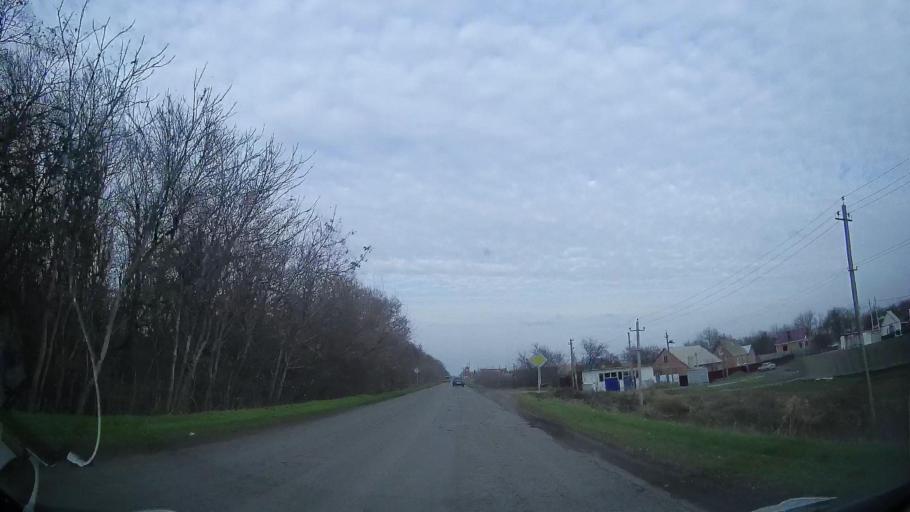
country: RU
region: Rostov
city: Zernograd
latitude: 46.8684
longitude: 40.3288
